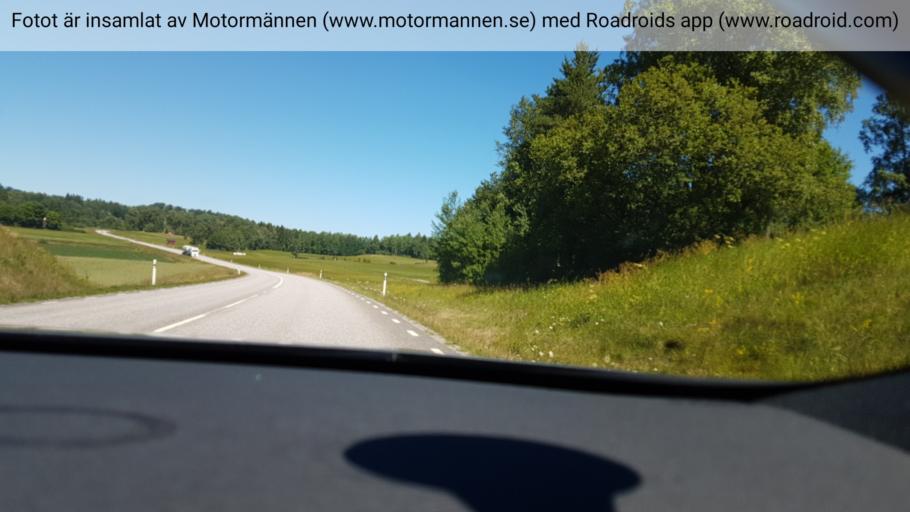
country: SE
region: Vaestra Goetaland
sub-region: Ulricehamns Kommun
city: Ulricehamn
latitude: 57.8754
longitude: 13.4344
